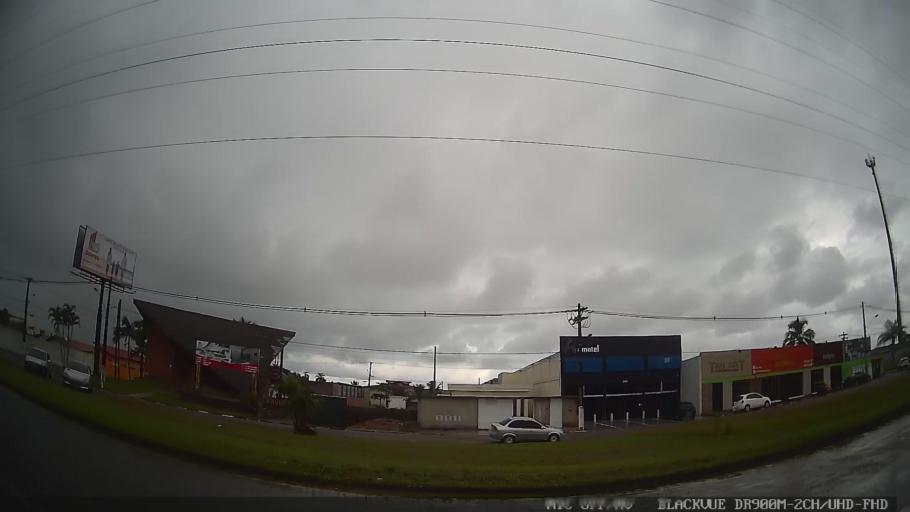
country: BR
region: Sao Paulo
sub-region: Itanhaem
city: Itanhaem
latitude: -24.1920
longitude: -46.8317
